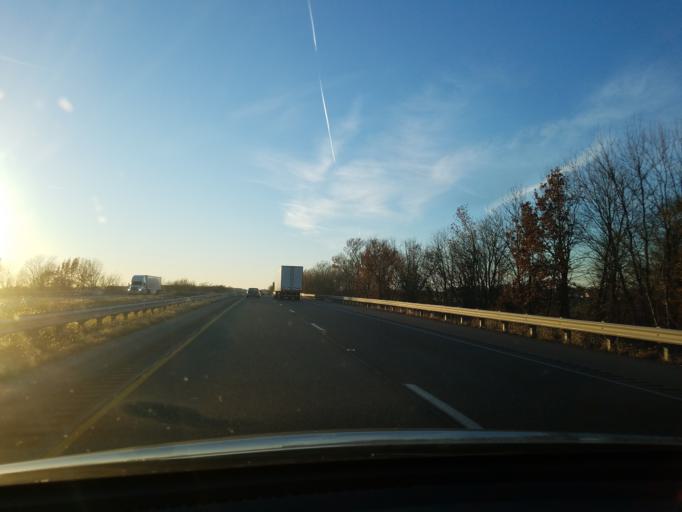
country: US
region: Indiana
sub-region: Gibson County
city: Haubstadt
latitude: 38.1672
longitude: -87.5632
